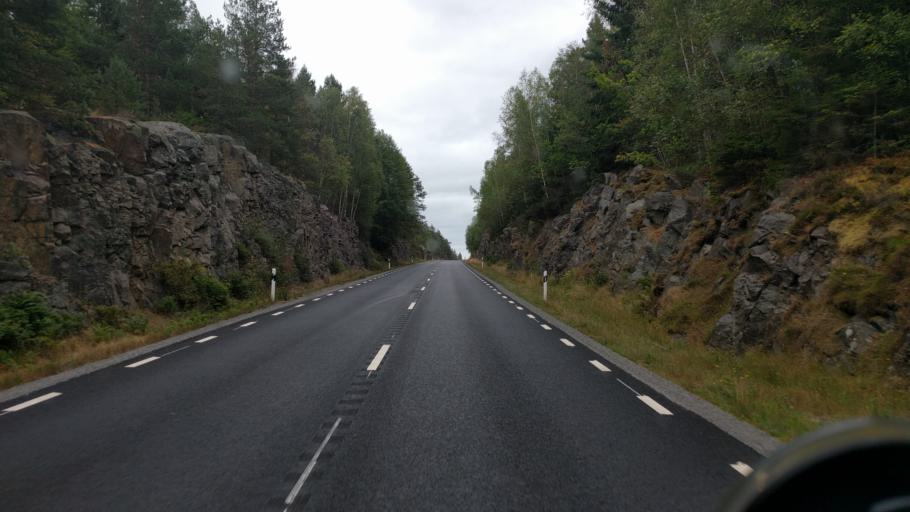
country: SE
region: Kalmar
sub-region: Vasterviks Kommun
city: Ankarsrum
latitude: 57.7240
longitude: 16.4072
